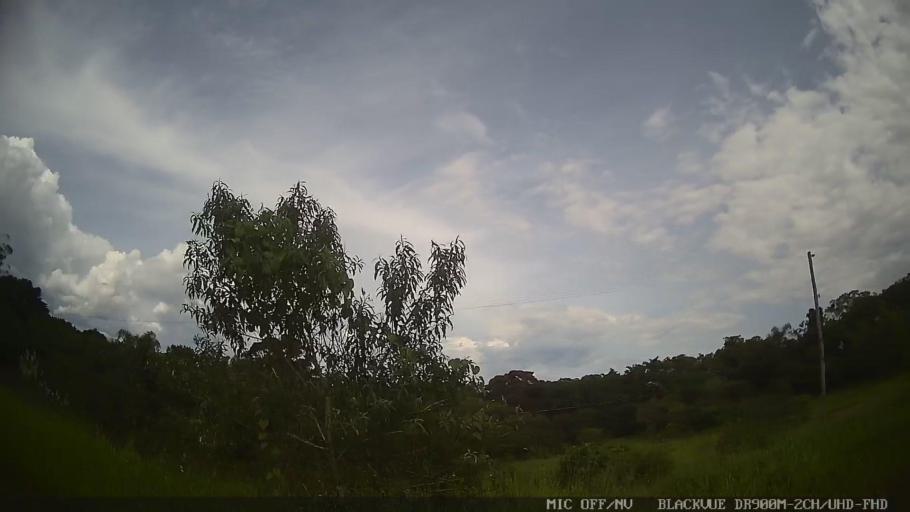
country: BR
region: Sao Paulo
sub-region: Suzano
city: Suzano
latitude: -23.6667
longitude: -46.2459
